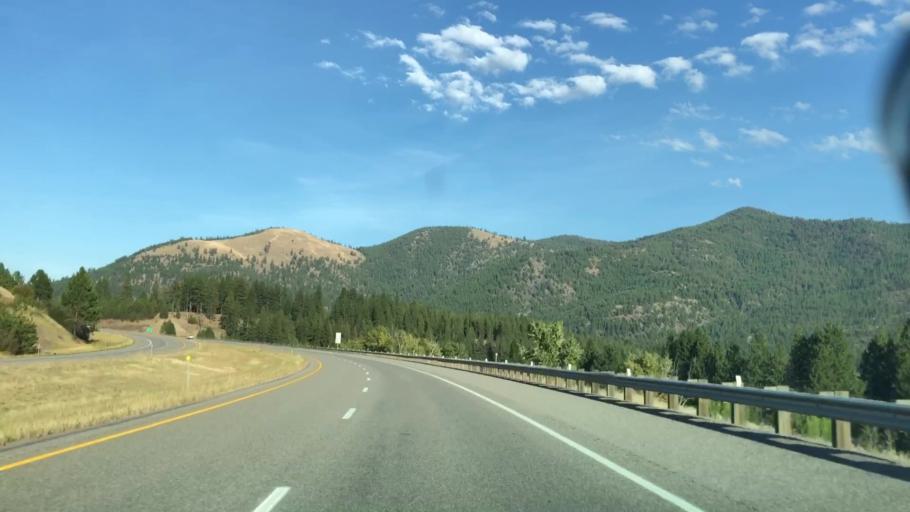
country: US
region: Montana
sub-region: Missoula County
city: Frenchtown
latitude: 46.9908
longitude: -114.4340
